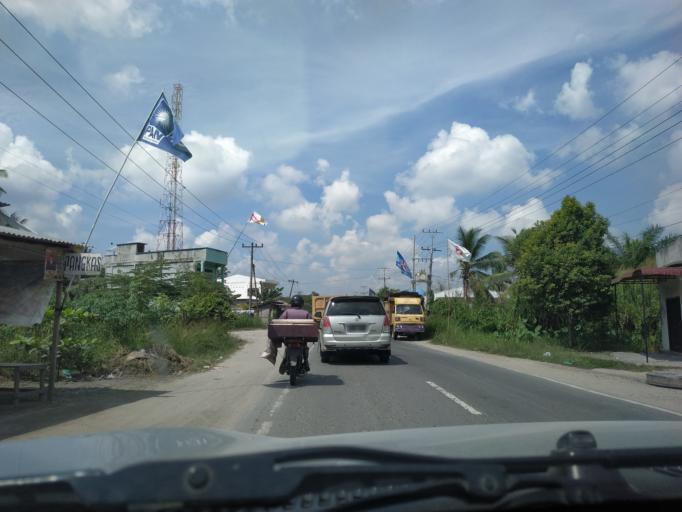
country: ID
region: North Sumatra
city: Tanjungbalai
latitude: 2.9236
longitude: 99.7336
